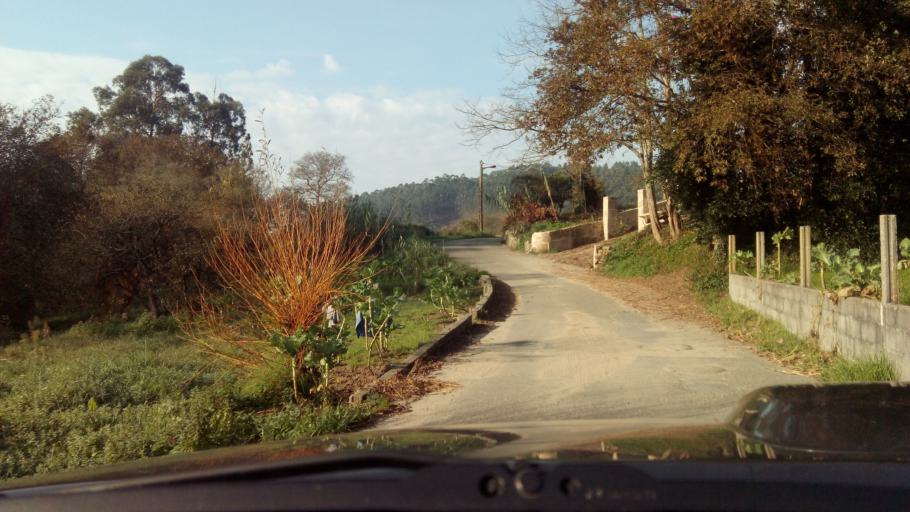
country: ES
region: Galicia
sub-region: Provincia de Pontevedra
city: Marin
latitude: 42.3639
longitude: -8.7332
